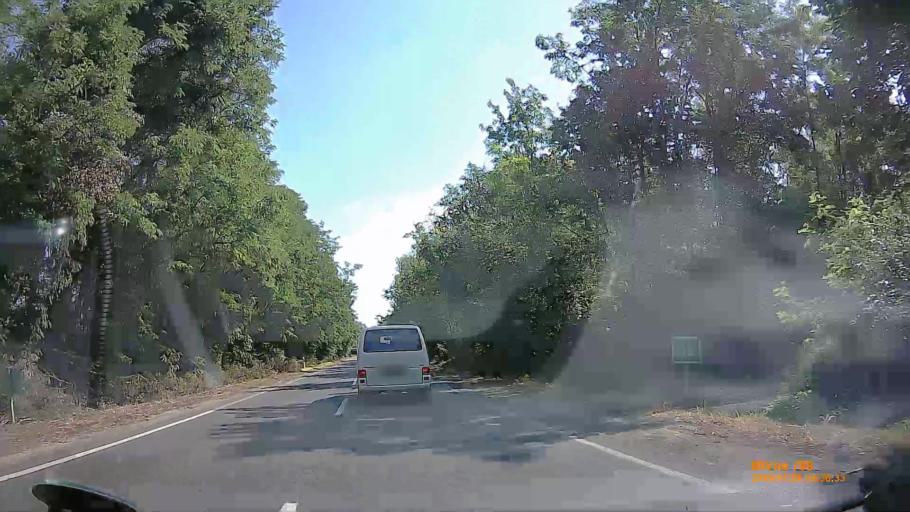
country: HU
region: Szabolcs-Szatmar-Bereg
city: Nyirmada
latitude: 48.0659
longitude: 22.2257
